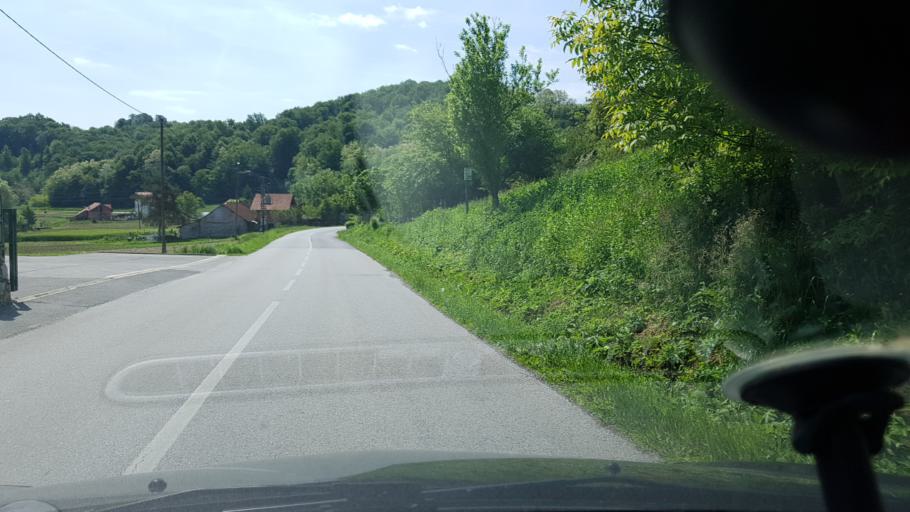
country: HR
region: Krapinsko-Zagorska
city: Zabok
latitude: 46.0547
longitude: 15.9420
